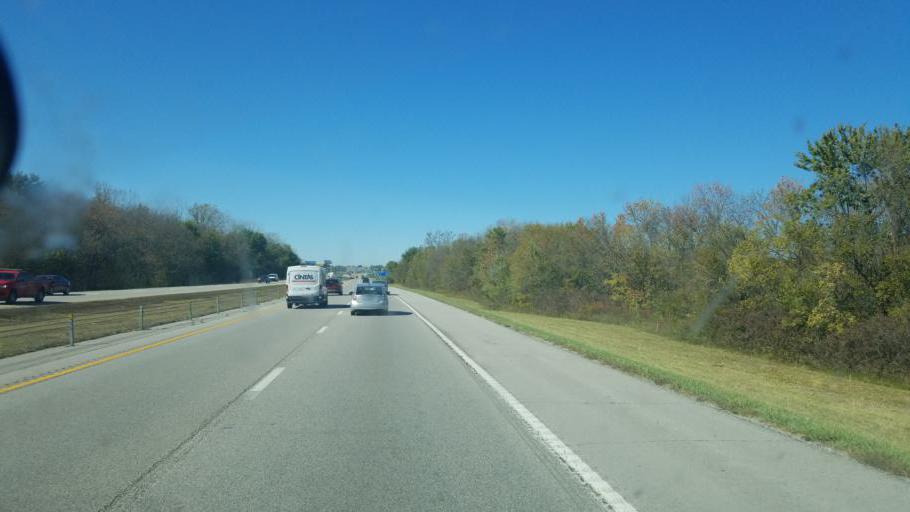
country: US
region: Missouri
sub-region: Jackson County
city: Grain Valley
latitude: 39.0204
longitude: -94.1773
